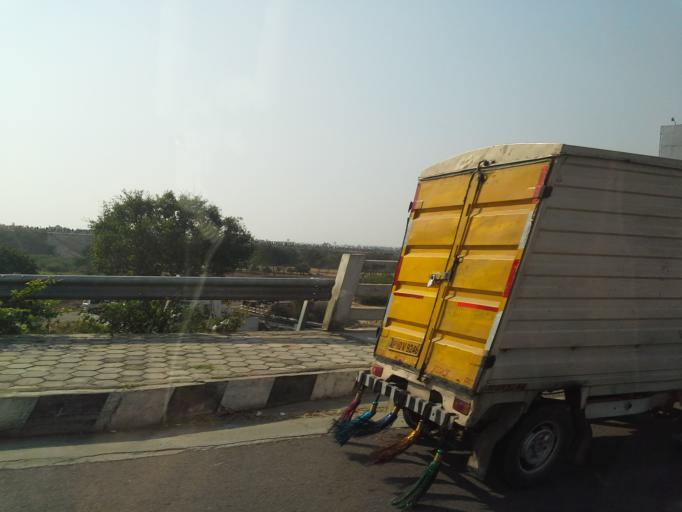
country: IN
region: Telangana
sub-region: Rangareddi
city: Sriramnagar
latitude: 17.2492
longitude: 78.3827
